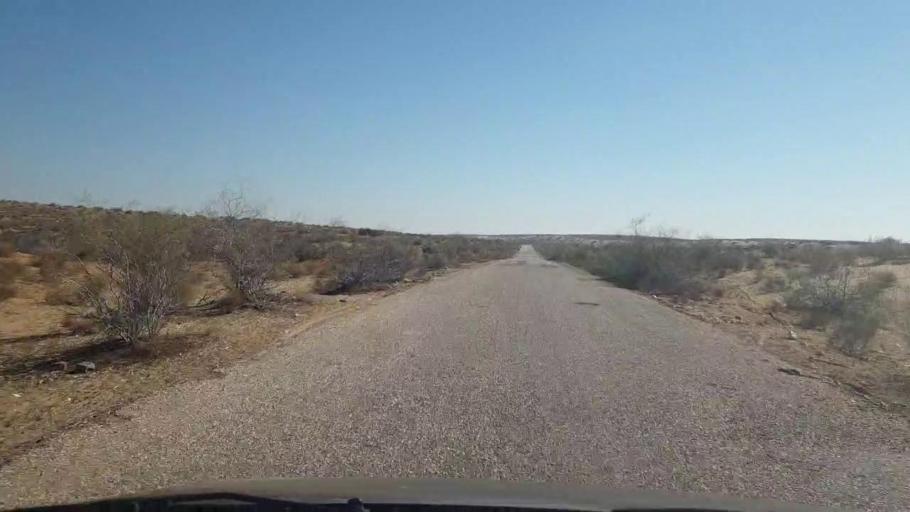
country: PK
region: Sindh
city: Bozdar
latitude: 27.0262
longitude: 68.7109
